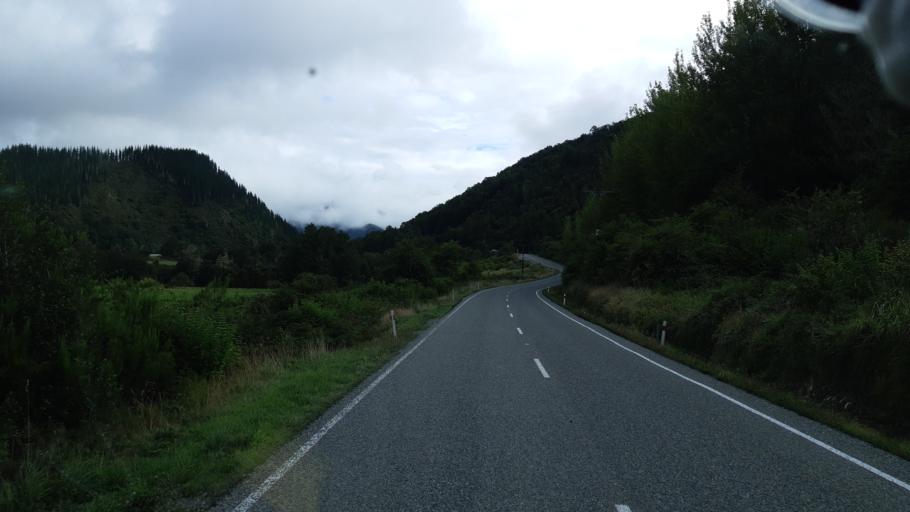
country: NZ
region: West Coast
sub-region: Buller District
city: Westport
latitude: -41.9693
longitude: 172.2039
